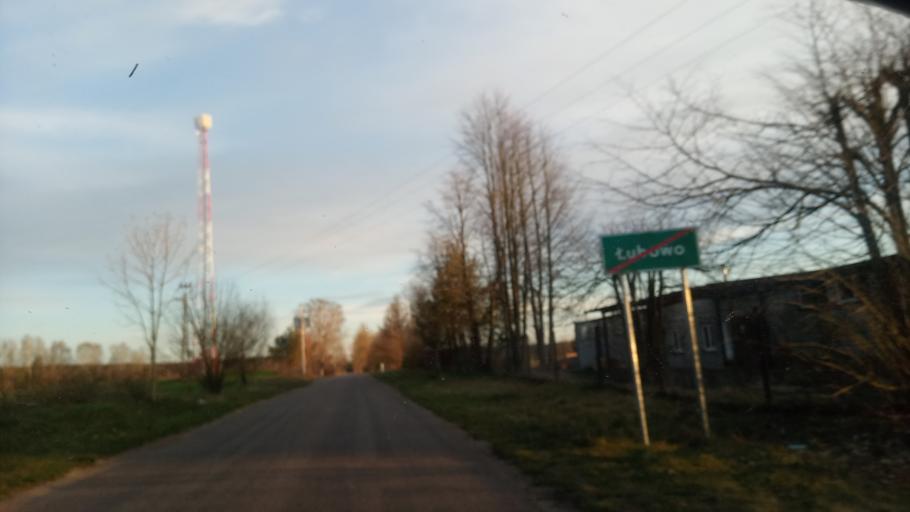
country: PL
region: West Pomeranian Voivodeship
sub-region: Powiat szczecinecki
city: Lubowo
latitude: 53.5835
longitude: 16.3934
